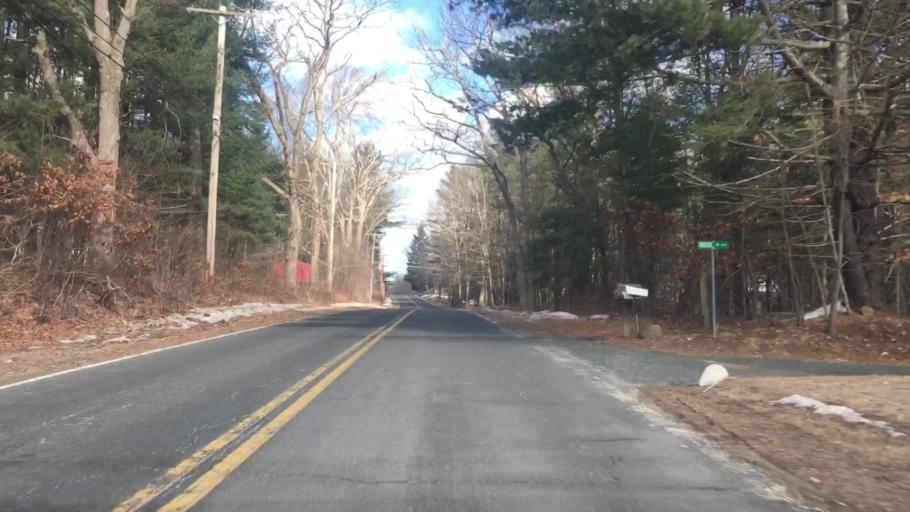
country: US
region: Massachusetts
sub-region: Hampden County
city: Wales
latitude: 42.0549
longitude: -72.2265
